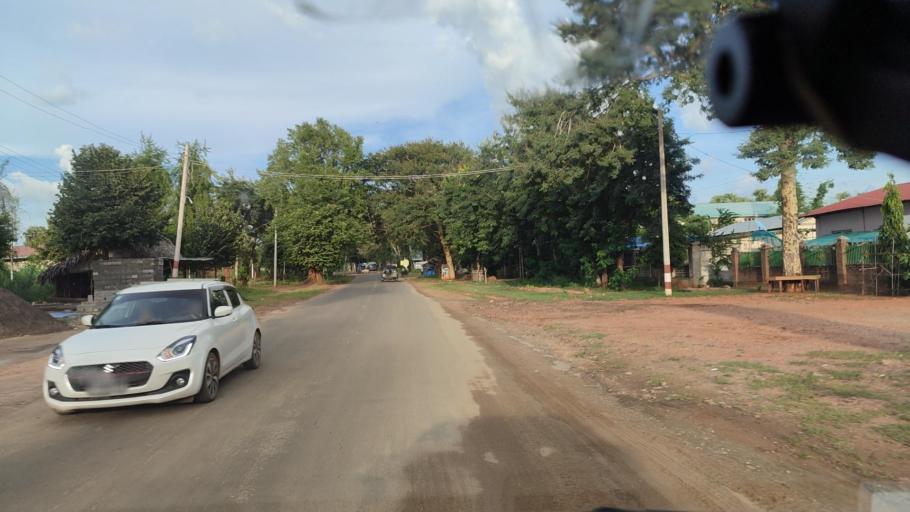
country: MM
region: Magway
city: Chauk
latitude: 20.8279
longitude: 95.1003
